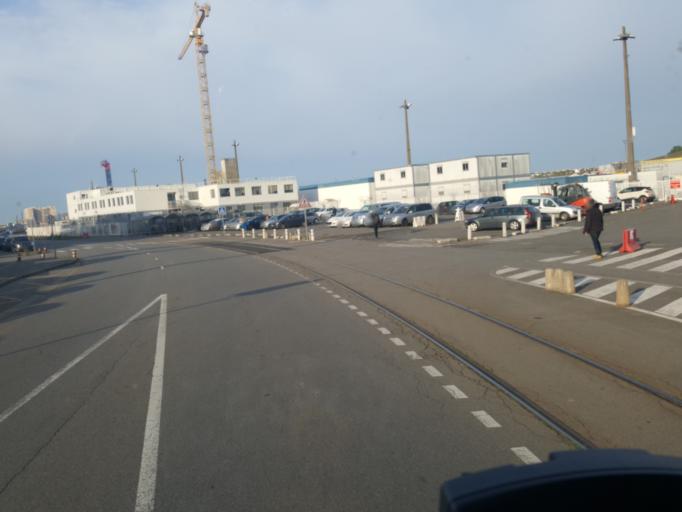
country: FR
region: Pays de la Loire
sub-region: Departement de la Loire-Atlantique
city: Saint-Nazaire
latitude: 47.2867
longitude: -2.1954
